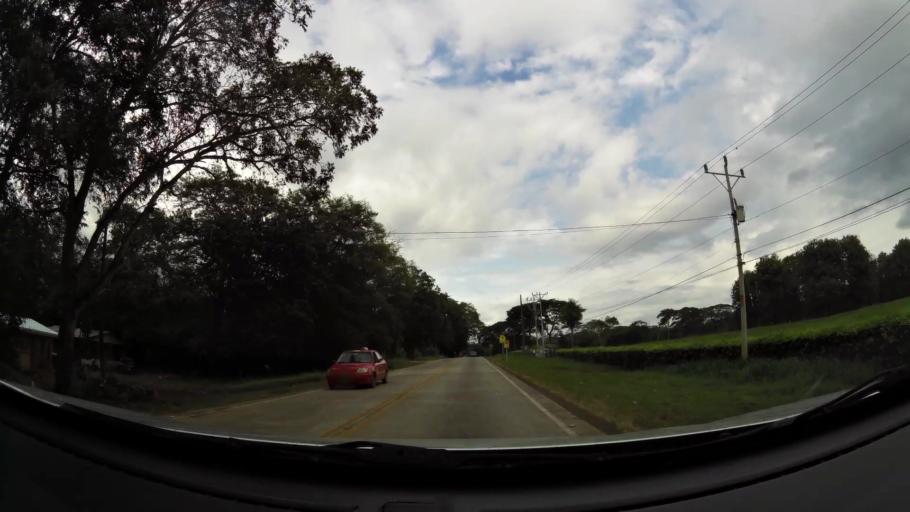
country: CR
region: Guanacaste
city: Juntas
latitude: 10.2490
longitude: -85.0612
